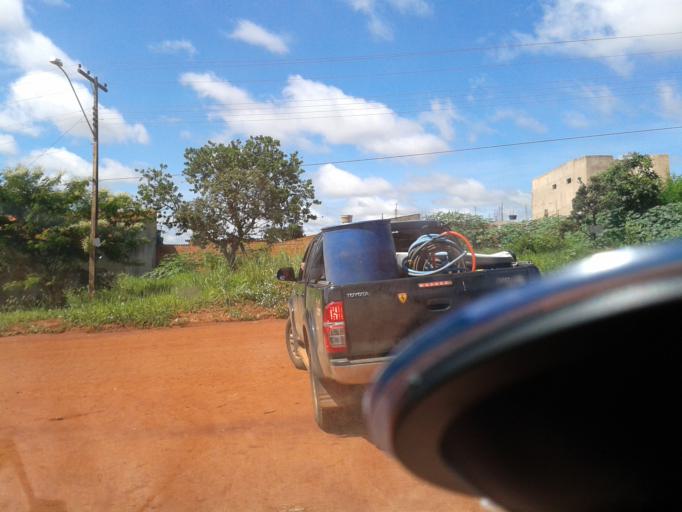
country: BR
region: Goias
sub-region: Goiania
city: Goiania
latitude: -16.6479
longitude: -49.3554
